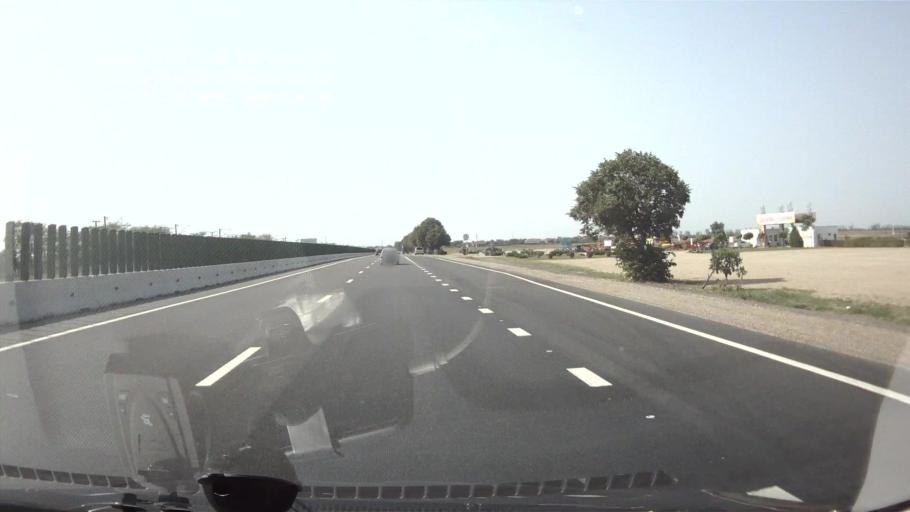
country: RU
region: Adygeya
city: Khatukay
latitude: 45.2196
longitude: 39.6031
